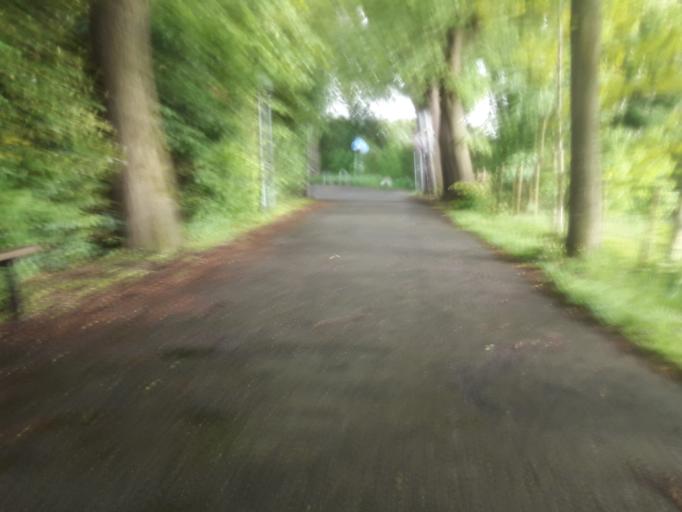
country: DE
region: North Rhine-Westphalia
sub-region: Regierungsbezirk Dusseldorf
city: Meerbusch
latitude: 51.2980
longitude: 6.7326
